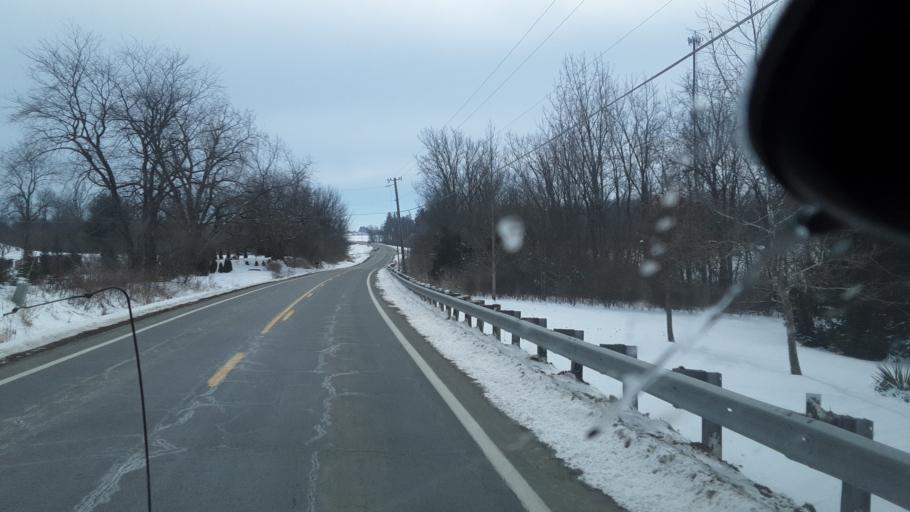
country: US
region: Ohio
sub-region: Madison County
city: Choctaw Lake
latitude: 39.9507
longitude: -83.5039
